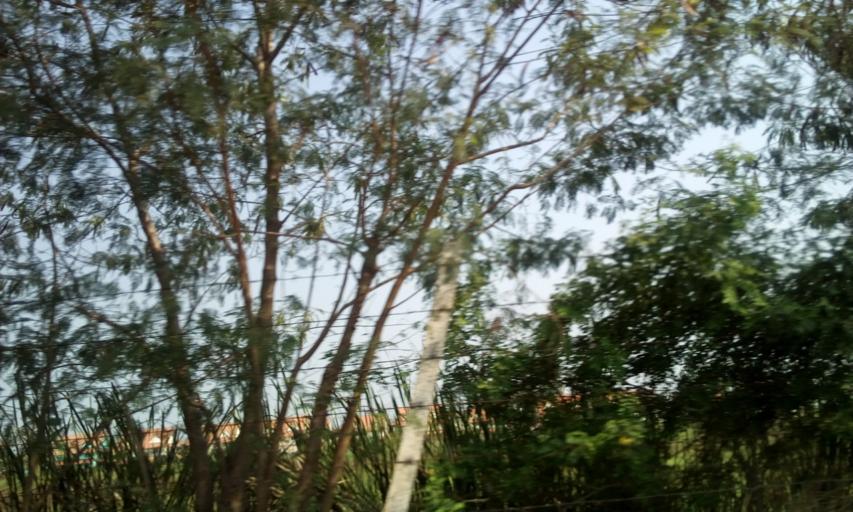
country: TH
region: Pathum Thani
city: Ban Rangsit
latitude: 14.0203
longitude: 100.7592
